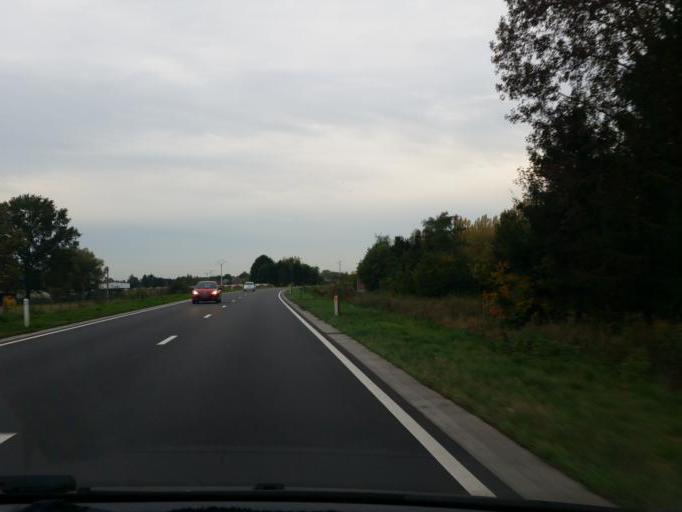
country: BE
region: Flanders
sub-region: Provincie Antwerpen
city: Sint-Katelijne-Waver
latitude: 51.0489
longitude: 4.5279
